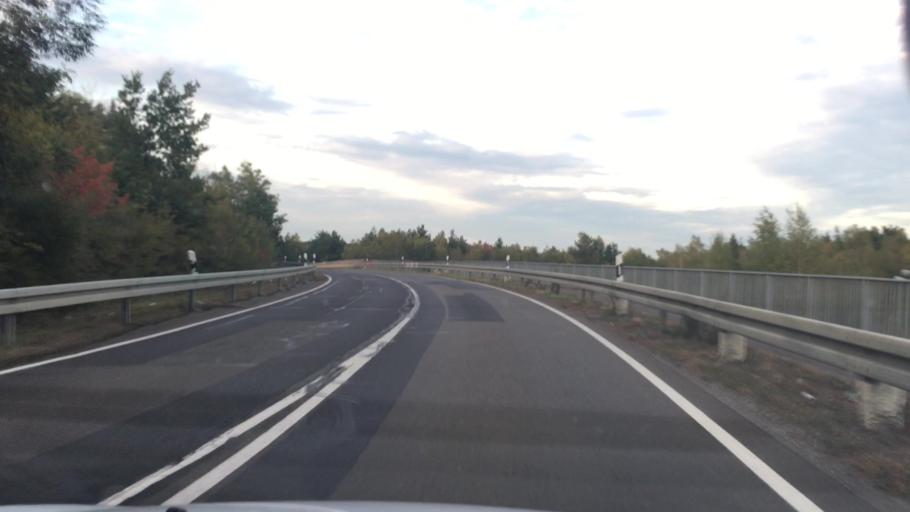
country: DE
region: Brandenburg
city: Schipkau
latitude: 51.4890
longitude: 13.8903
